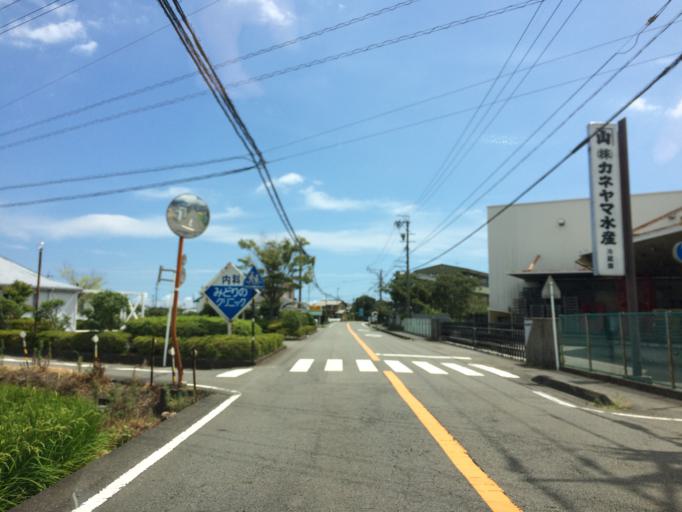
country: JP
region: Shizuoka
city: Yaizu
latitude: 34.8865
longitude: 138.3126
